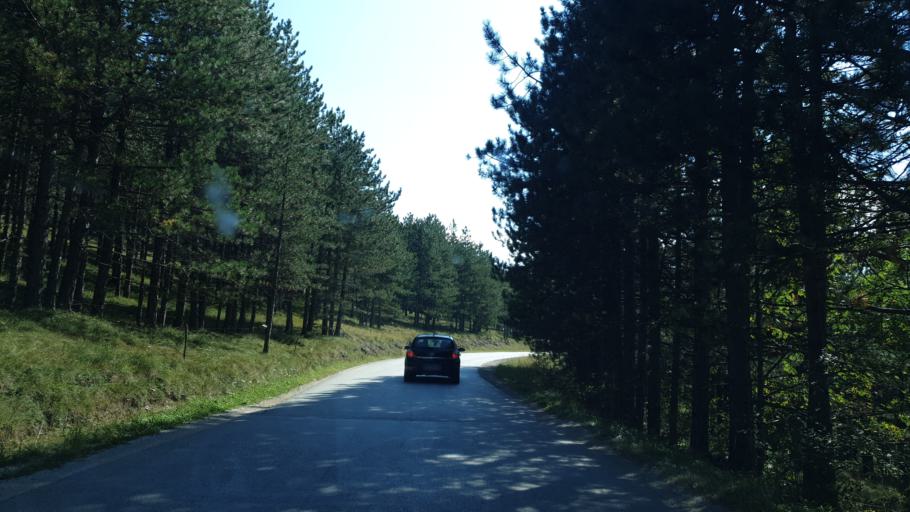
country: RS
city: Zlatibor
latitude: 43.7202
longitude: 19.7225
